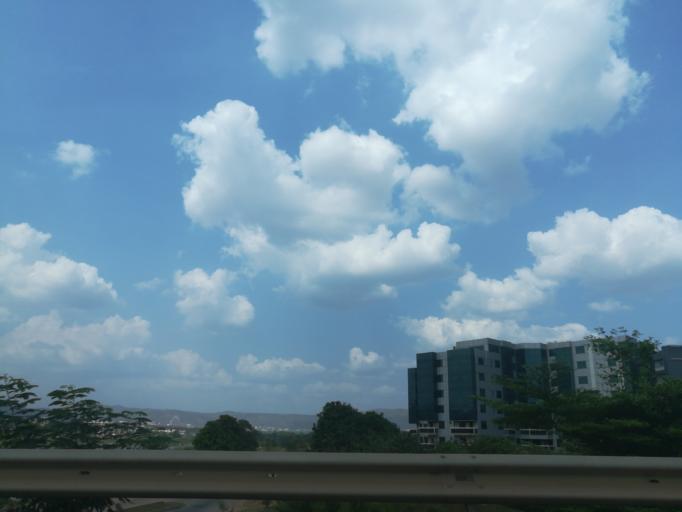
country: NG
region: Abuja Federal Capital Territory
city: Abuja
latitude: 9.0789
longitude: 7.4286
